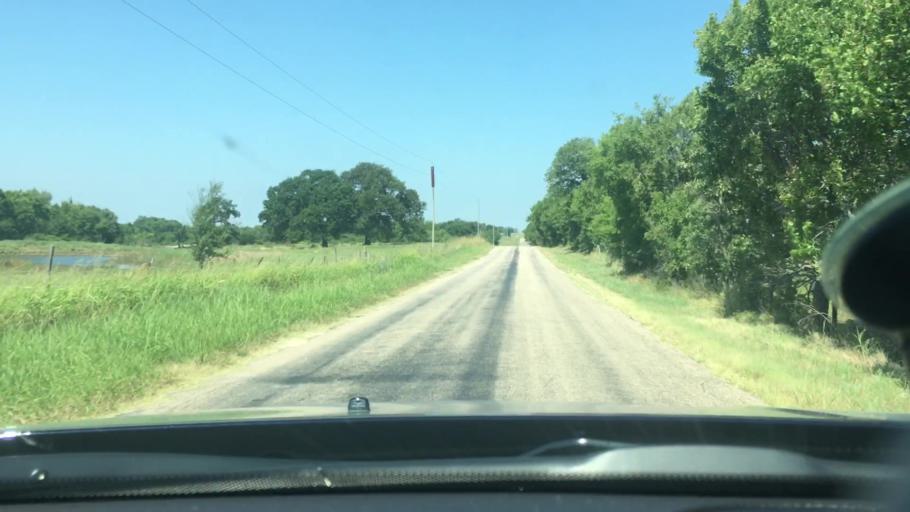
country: US
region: Oklahoma
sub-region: Johnston County
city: Tishomingo
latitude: 34.3177
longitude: -96.6617
